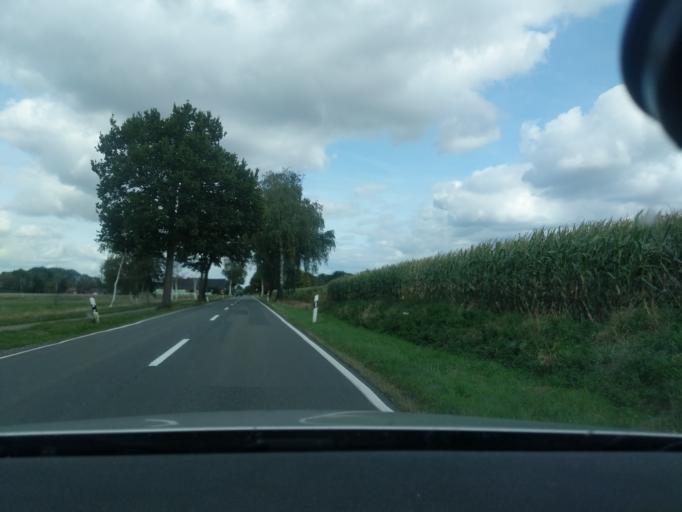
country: DE
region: Lower Saxony
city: Warpe
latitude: 52.7477
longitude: 9.0726
